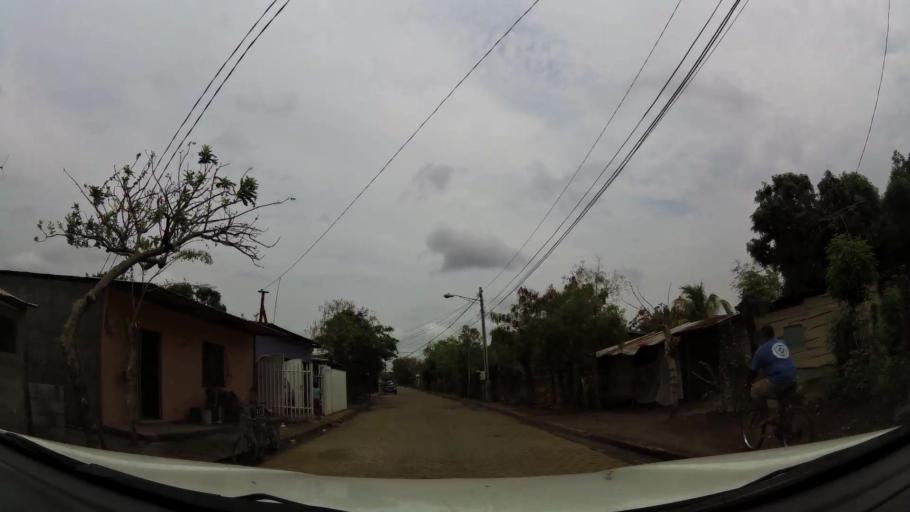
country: NI
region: Granada
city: Granada
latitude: 11.9147
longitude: -85.9564
